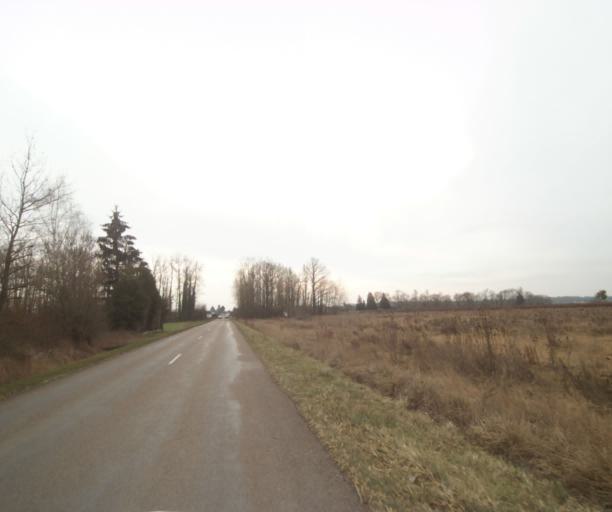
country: FR
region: Champagne-Ardenne
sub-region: Departement de la Haute-Marne
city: Villiers-en-Lieu
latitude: 48.6723
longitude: 4.8912
